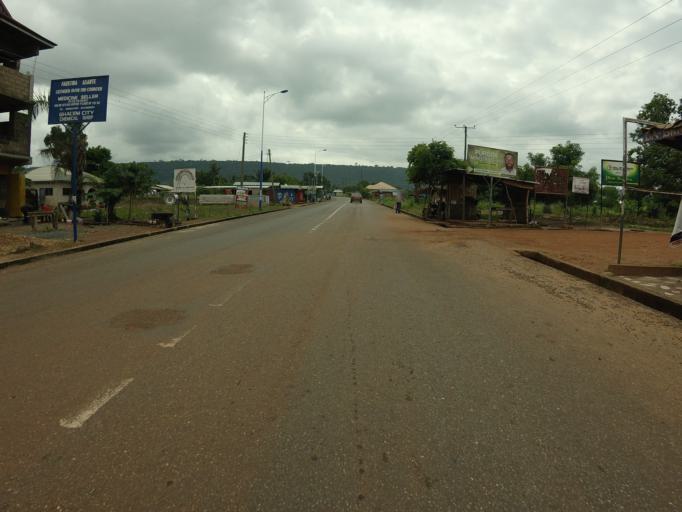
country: GH
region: Volta
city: Ho
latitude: 6.6286
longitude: 0.4886
